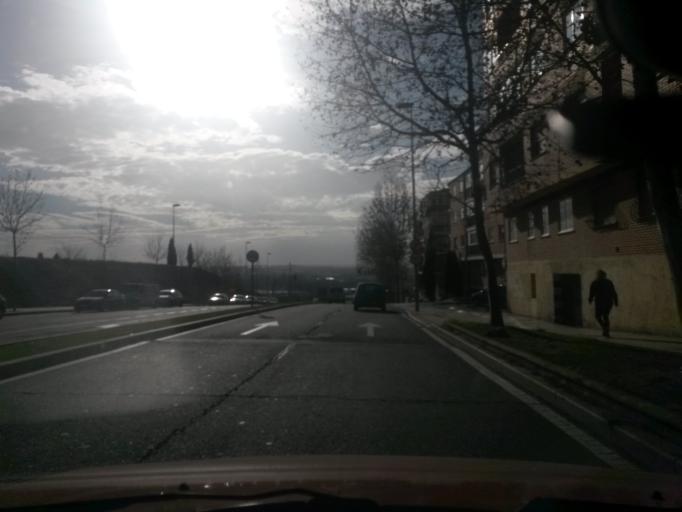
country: ES
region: Castille and Leon
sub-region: Provincia de Salamanca
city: Salamanca
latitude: 40.9688
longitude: -5.6437
